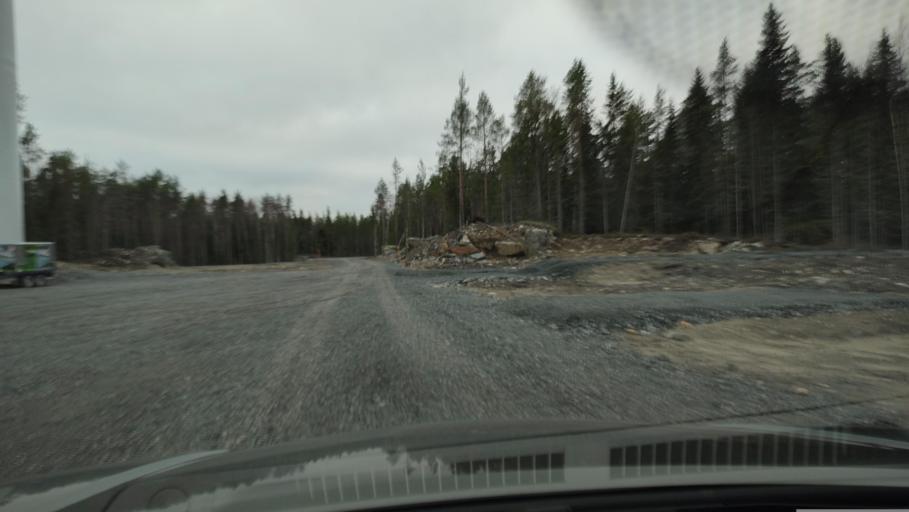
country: FI
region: Ostrobothnia
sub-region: Sydosterbotten
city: Kristinestad
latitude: 62.1951
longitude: 21.5511
